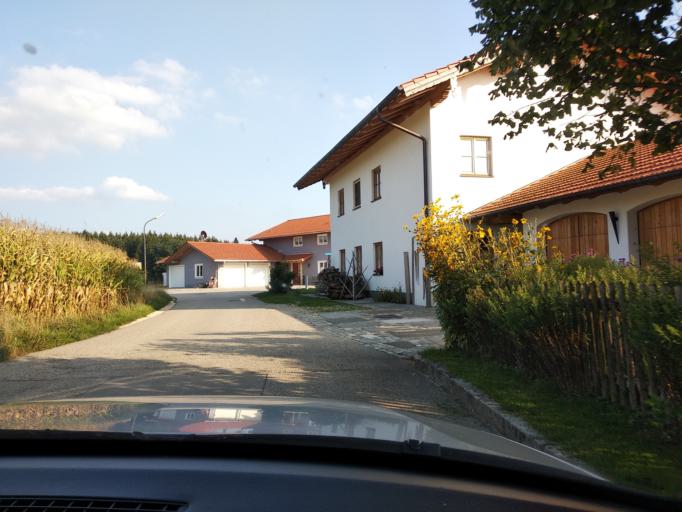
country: DE
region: Bavaria
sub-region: Upper Bavaria
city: Obing
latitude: 47.9974
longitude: 12.4155
